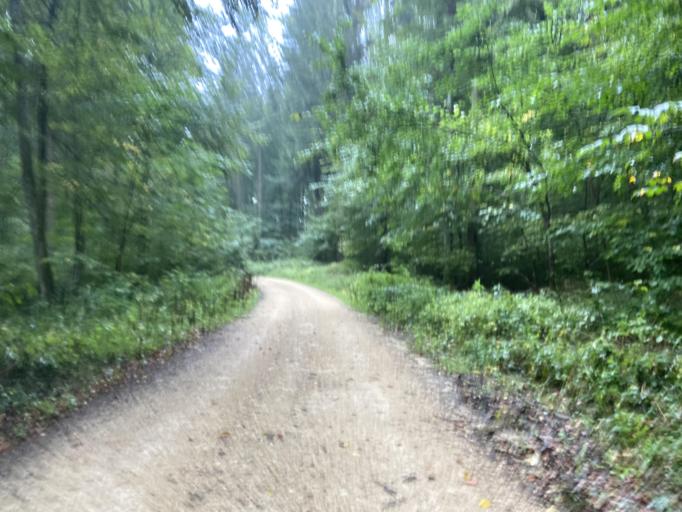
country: DE
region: Baden-Wuerttemberg
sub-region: Tuebingen Region
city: Bingen
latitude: 48.1280
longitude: 9.2574
